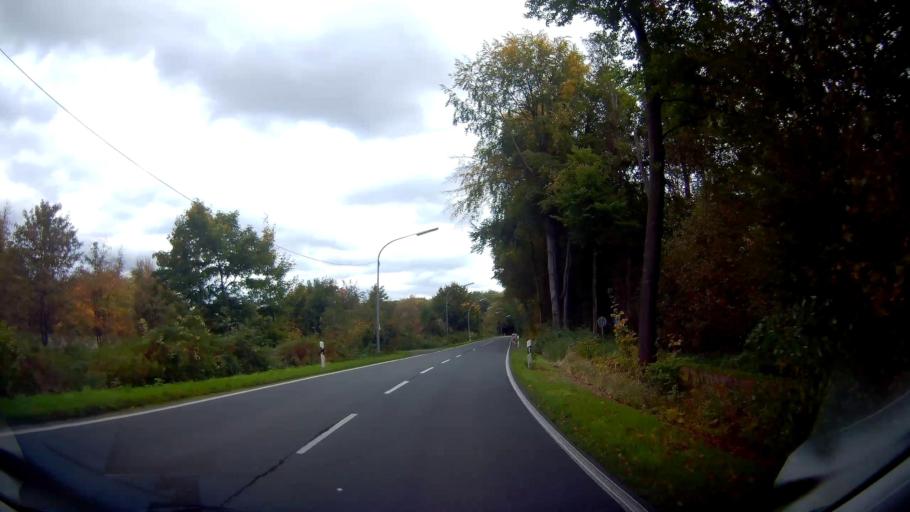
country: DE
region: North Rhine-Westphalia
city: Marl
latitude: 51.5866
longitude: 7.0712
